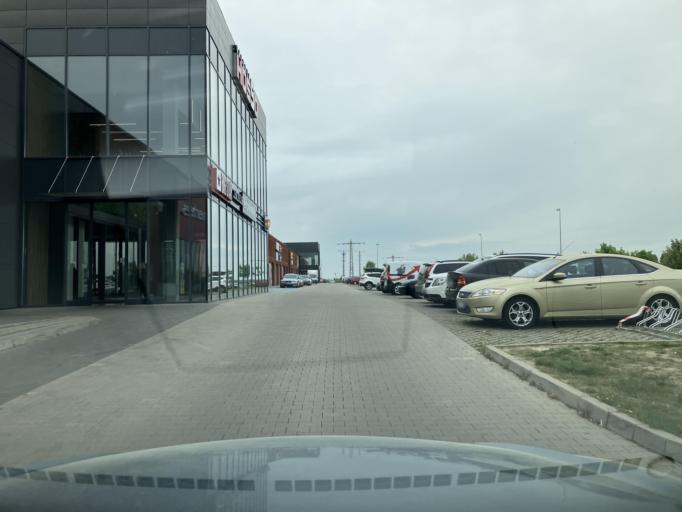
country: PL
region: Lubusz
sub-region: Powiat swiebodzinski
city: Swiebodzin
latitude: 52.2349
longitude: 15.5346
